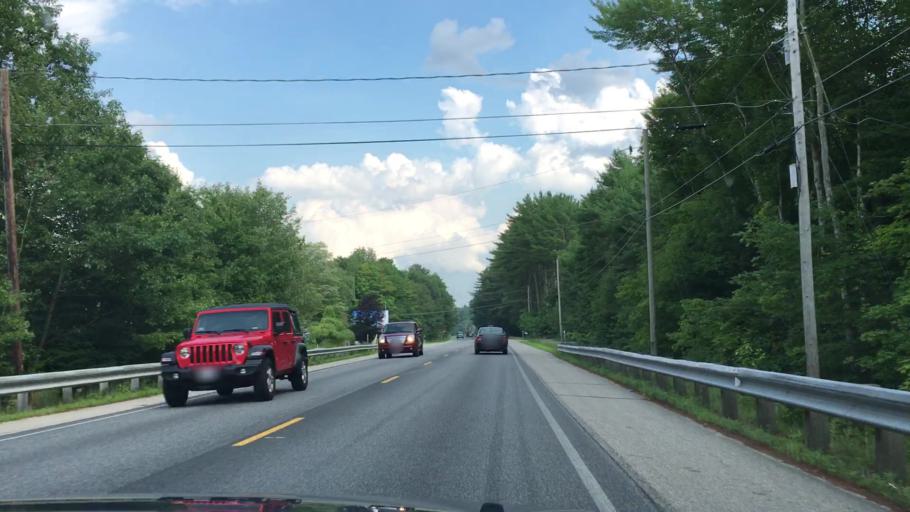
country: US
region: New Hampshire
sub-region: Strafford County
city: Farmington
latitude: 43.3915
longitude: -71.0914
